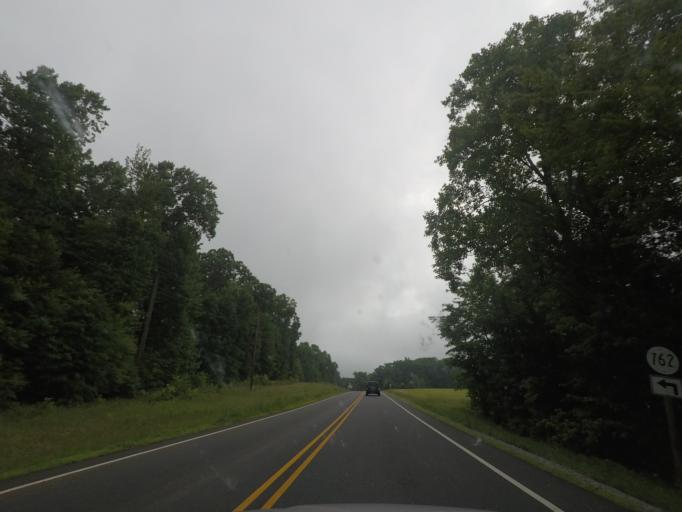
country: US
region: Virginia
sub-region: Prince Edward County
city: Hampden Sydney
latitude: 37.1086
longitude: -78.4677
